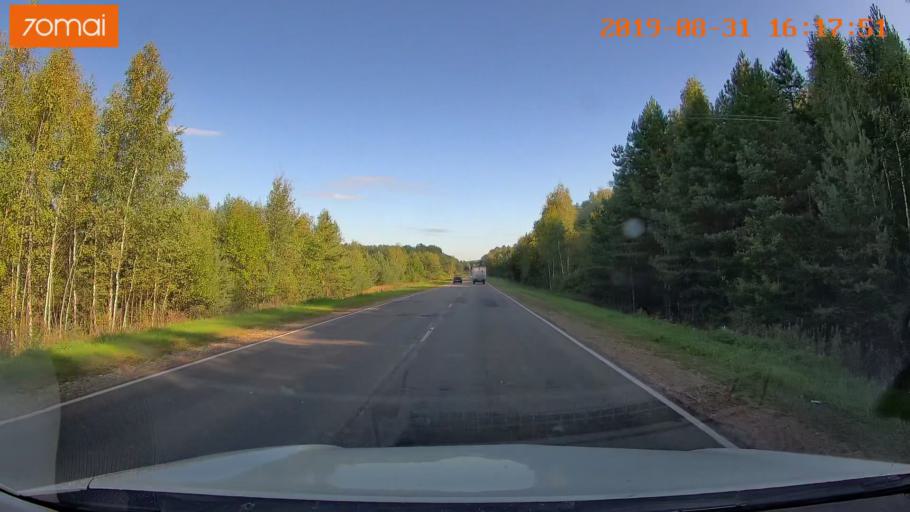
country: RU
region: Kaluga
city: Nikola-Lenivets
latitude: 54.5419
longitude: 35.5427
